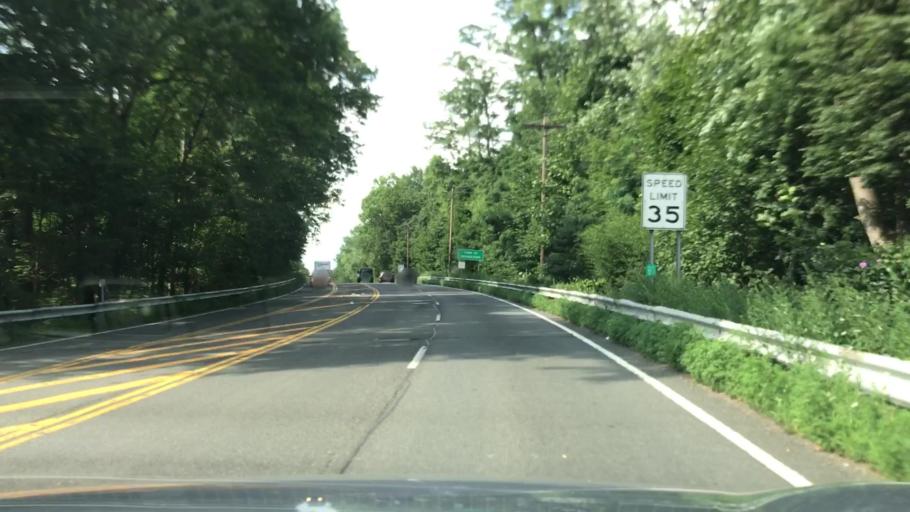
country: US
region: New York
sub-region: Rockland County
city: Tappan
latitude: 41.0199
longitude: -73.9422
